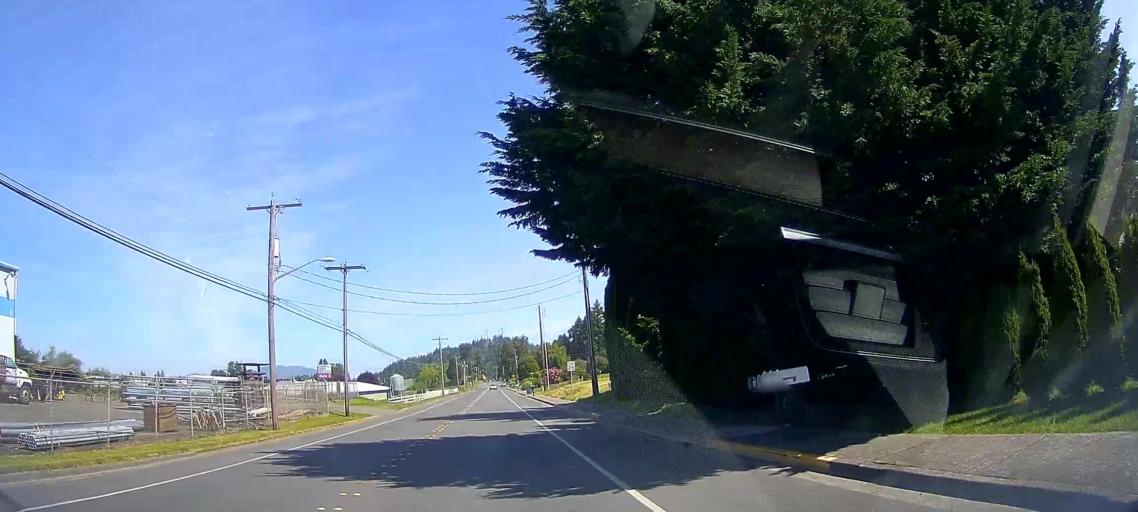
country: US
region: Washington
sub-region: Skagit County
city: Burlington
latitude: 48.4619
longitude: -122.3247
